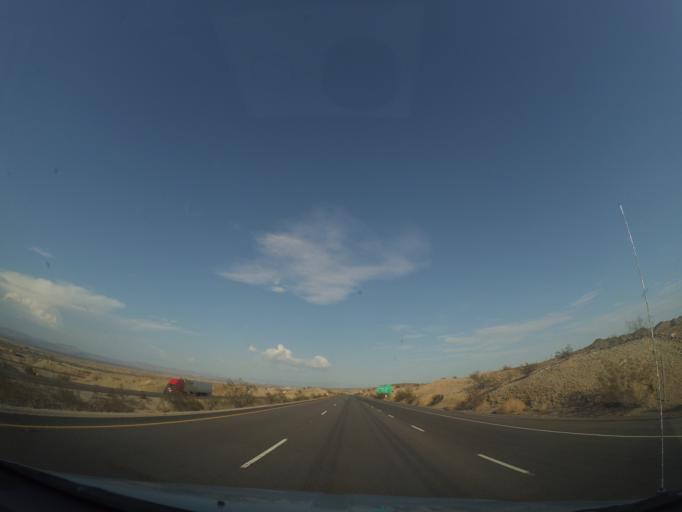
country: US
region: California
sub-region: San Bernardino County
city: Needles
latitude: 34.7176
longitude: -114.5068
